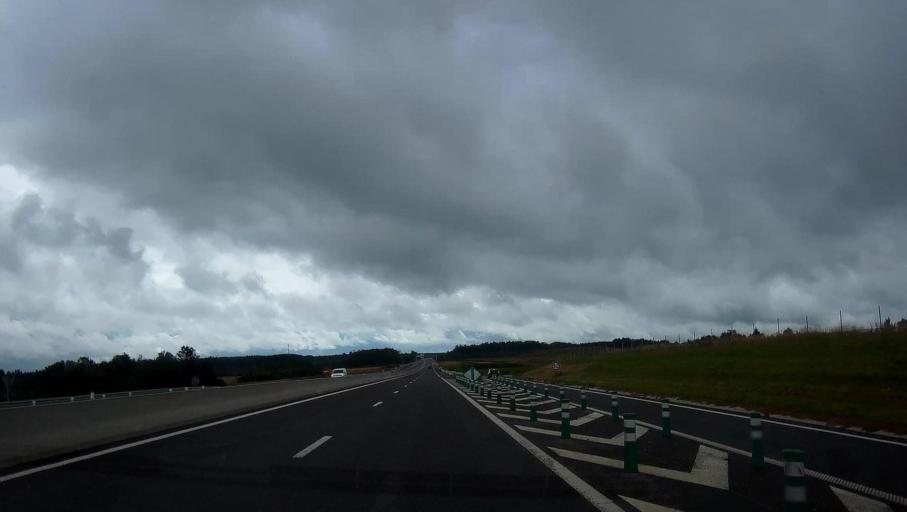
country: FR
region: Champagne-Ardenne
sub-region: Departement des Ardennes
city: Rocroi
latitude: 49.9061
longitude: 4.5221
